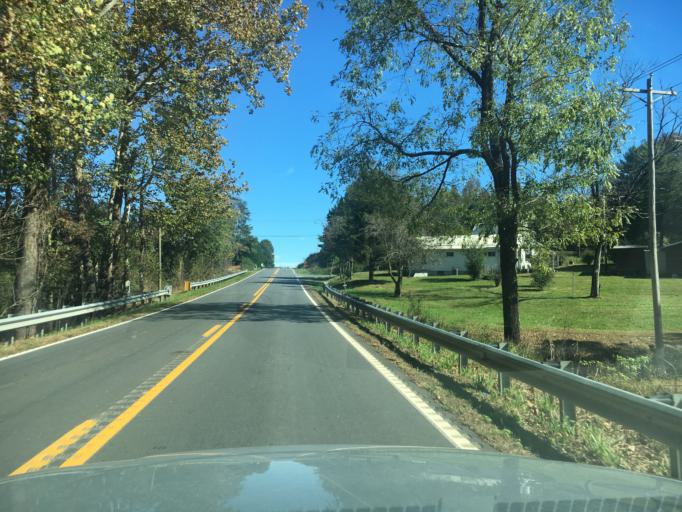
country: US
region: North Carolina
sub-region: Burke County
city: Glen Alpine
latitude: 35.6483
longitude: -81.7661
